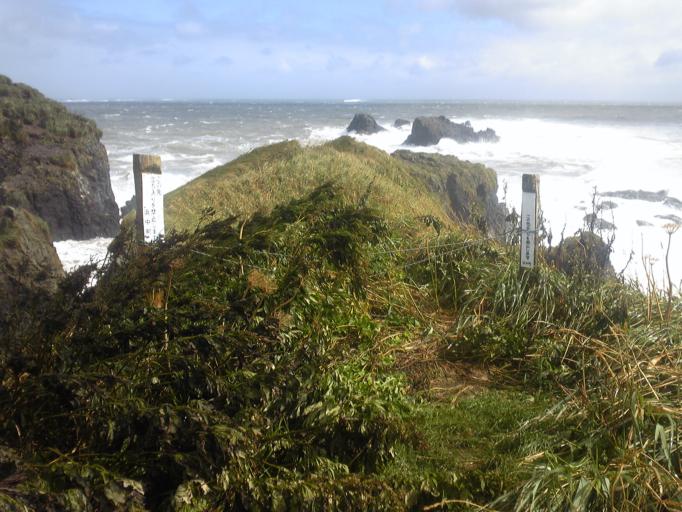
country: JP
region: Hokkaido
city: Nemuro
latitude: 43.0797
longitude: 145.1628
